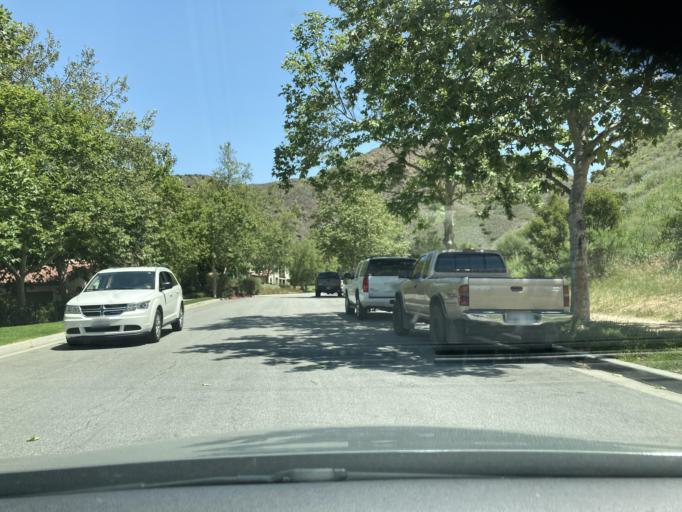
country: US
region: California
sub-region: Ventura County
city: Camarillo
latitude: 34.1627
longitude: -119.0352
